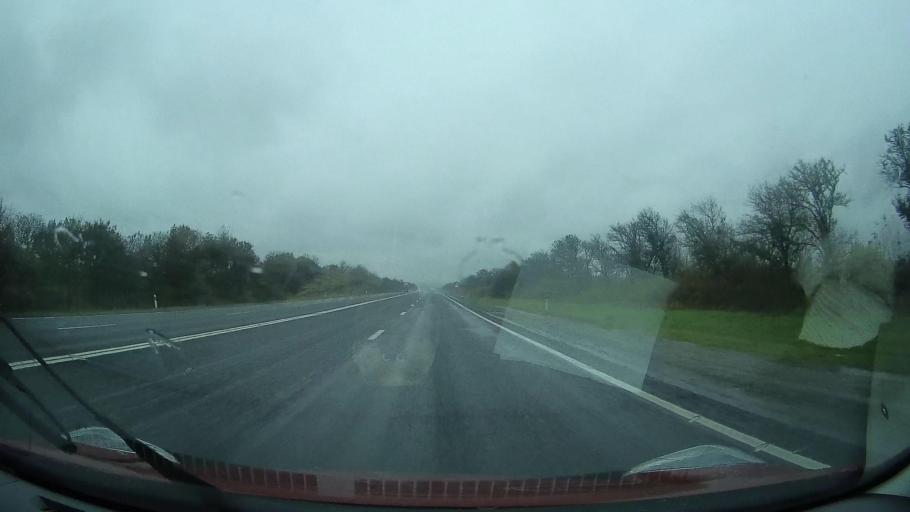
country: RU
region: Stavropol'skiy
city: Nevinnomyssk
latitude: 44.6164
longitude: 42.1043
